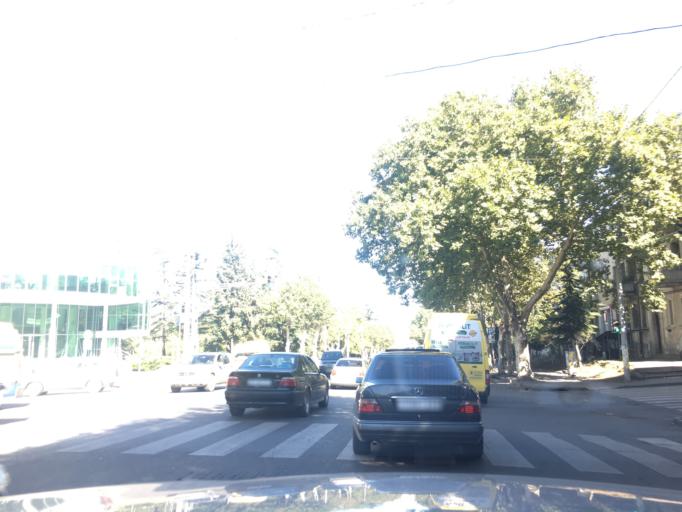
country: GE
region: T'bilisi
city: Tbilisi
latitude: 41.7464
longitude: 44.7921
